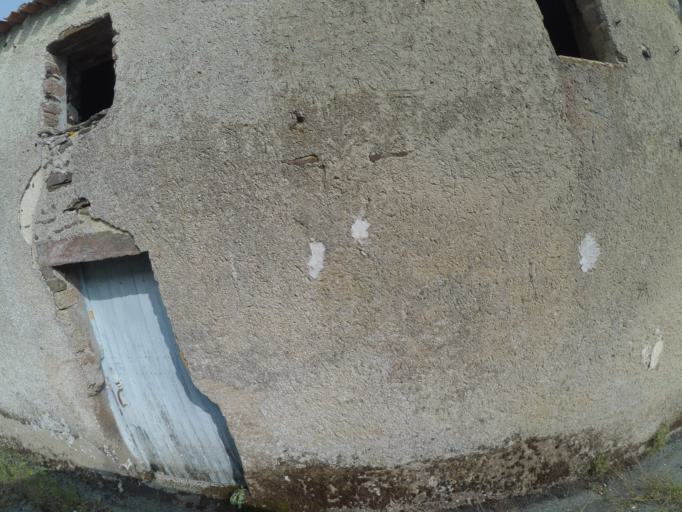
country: FR
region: Pays de la Loire
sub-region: Departement de la Vendee
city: Saint-Georges-de-Montaigu
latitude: 46.9502
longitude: -1.2967
